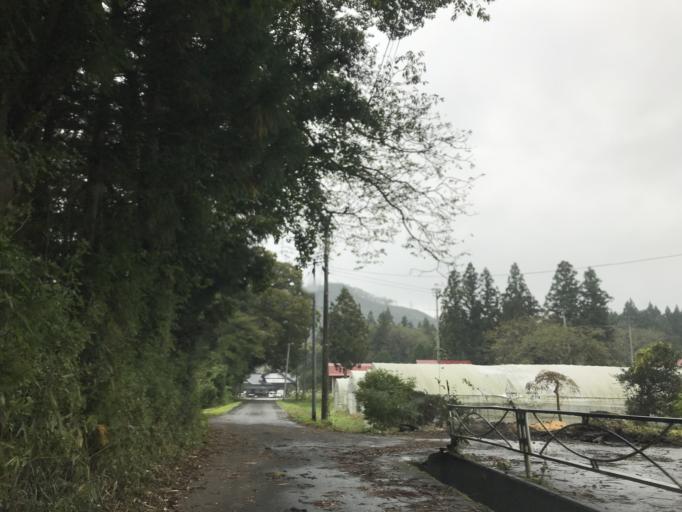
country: JP
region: Iwate
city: Ichinoseki
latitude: 38.9740
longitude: 140.9595
